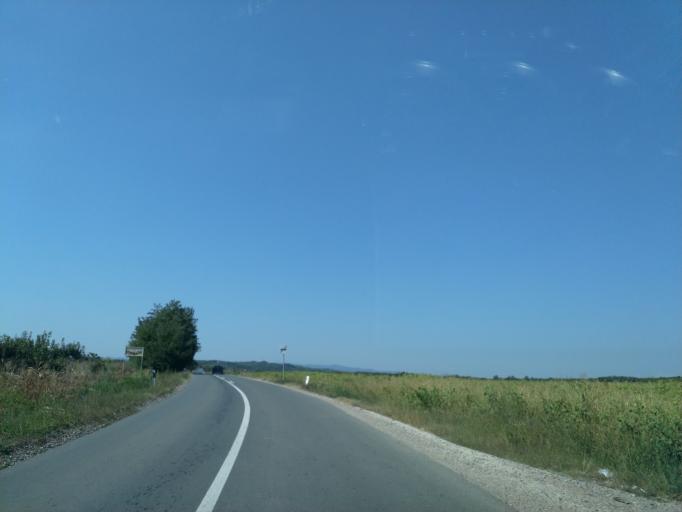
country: RS
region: Central Serbia
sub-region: Rasinski Okrug
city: Trstenik
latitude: 43.6277
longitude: 21.1564
